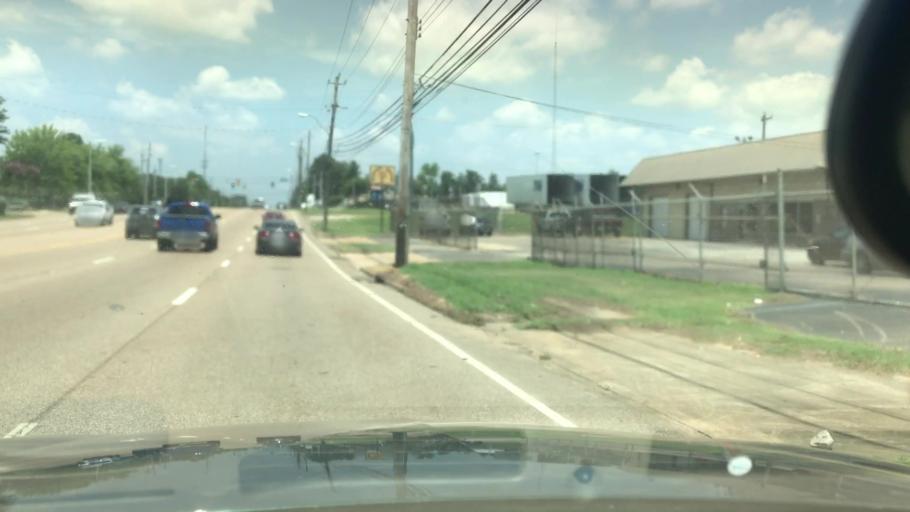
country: US
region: Mississippi
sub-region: De Soto County
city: Southaven
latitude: 35.0223
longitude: -89.9368
